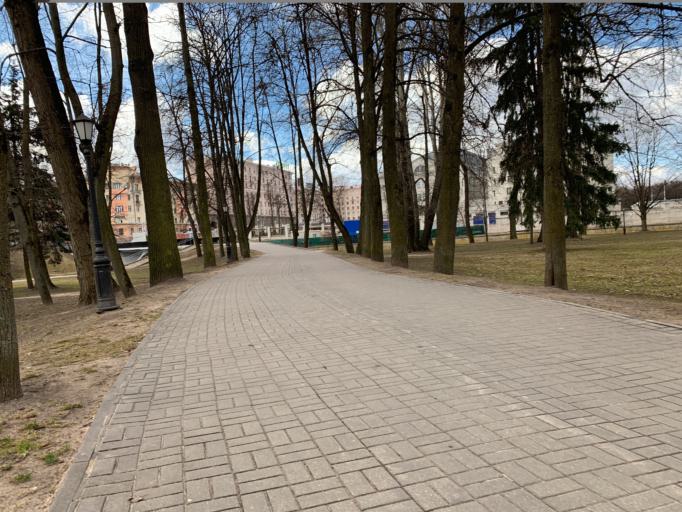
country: BY
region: Minsk
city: Minsk
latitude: 53.9029
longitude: 27.5703
